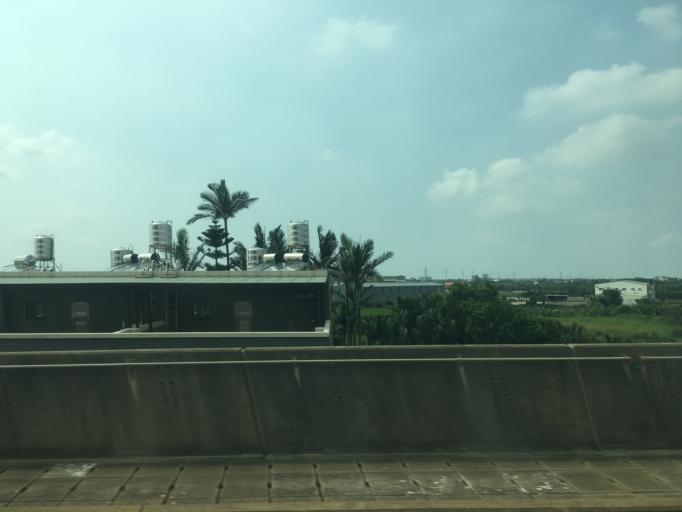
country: TW
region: Taiwan
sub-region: Hsinchu
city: Zhubei
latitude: 24.9488
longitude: 121.1346
